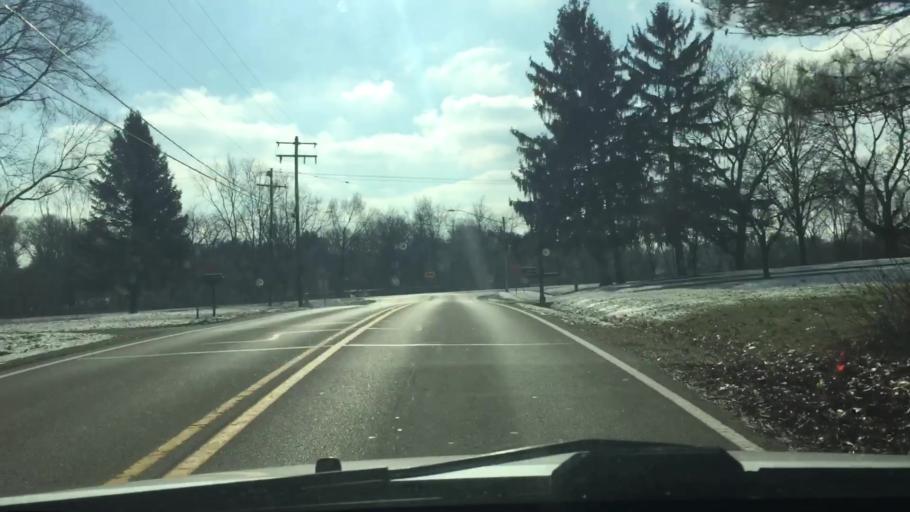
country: US
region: Wisconsin
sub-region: Waukesha County
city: Waukesha
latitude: 42.9780
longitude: -88.2873
